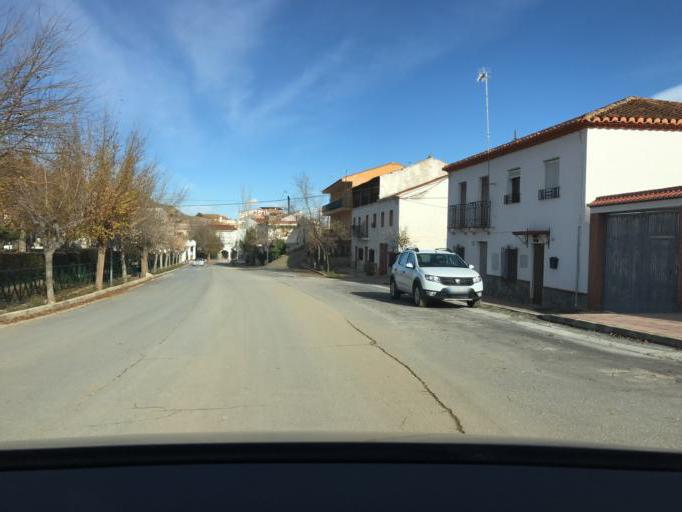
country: ES
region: Andalusia
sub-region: Provincia de Granada
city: Marchal
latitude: 37.3024
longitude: -3.2118
